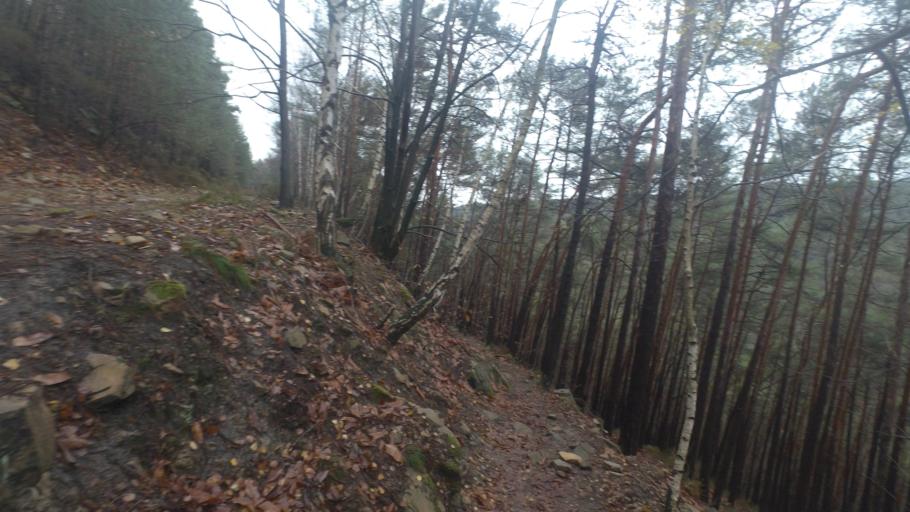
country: DE
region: Rheinland-Pfalz
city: Neustadt
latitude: 49.3822
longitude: 8.1399
